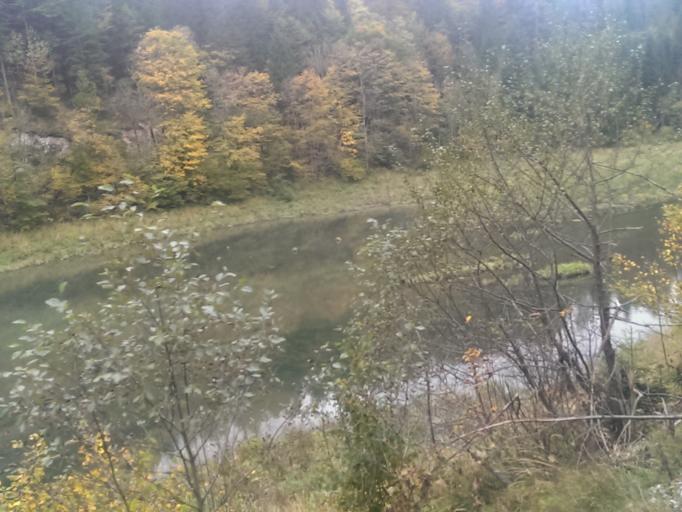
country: AT
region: Lower Austria
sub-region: Politischer Bezirk Lilienfeld
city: Mitterbach am Erlaufsee
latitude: 47.8576
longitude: 15.3023
